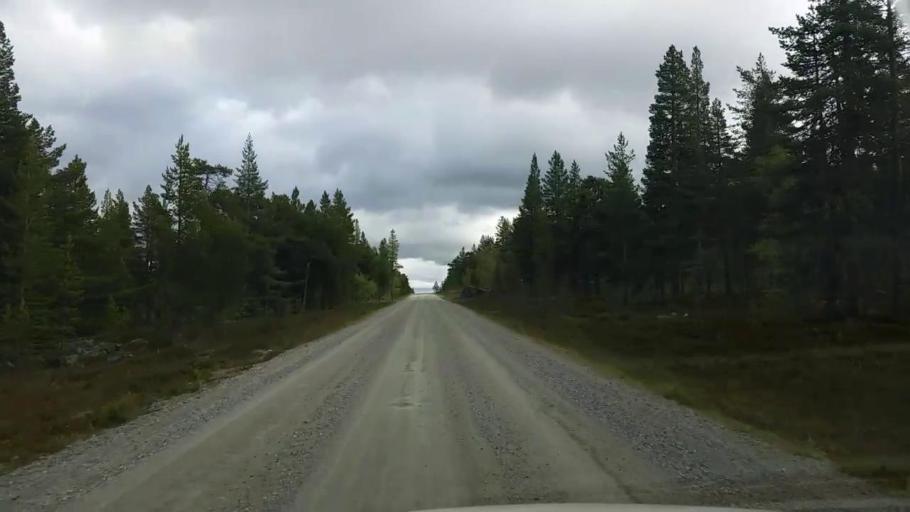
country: NO
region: Hedmark
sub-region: Engerdal
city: Engerdal
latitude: 62.3360
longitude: 12.6278
